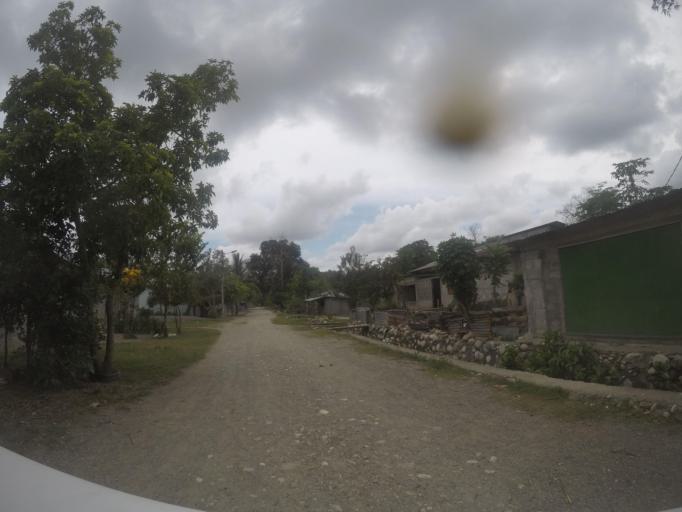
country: TL
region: Viqueque
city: Viqueque
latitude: -8.8785
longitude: 126.3633
